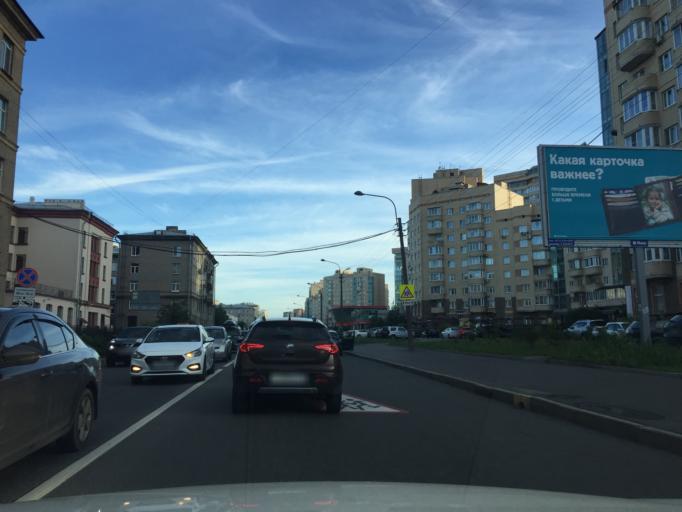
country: RU
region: St.-Petersburg
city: Admiralteisky
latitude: 59.8714
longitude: 30.3136
